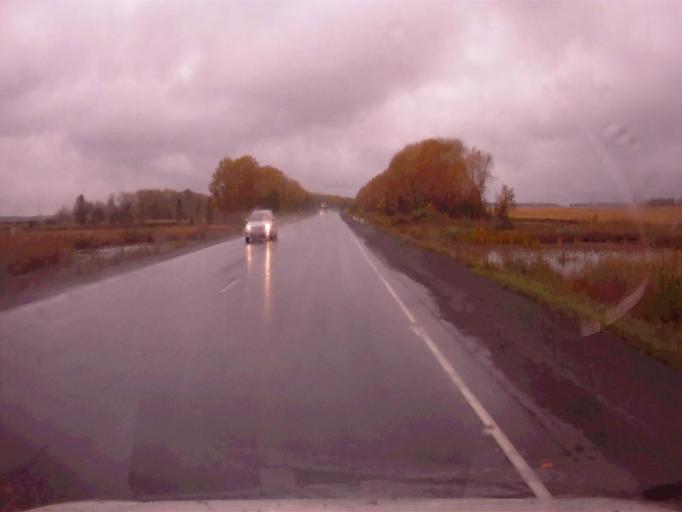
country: RU
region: Chelyabinsk
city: Argayash
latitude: 55.4473
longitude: 60.9463
